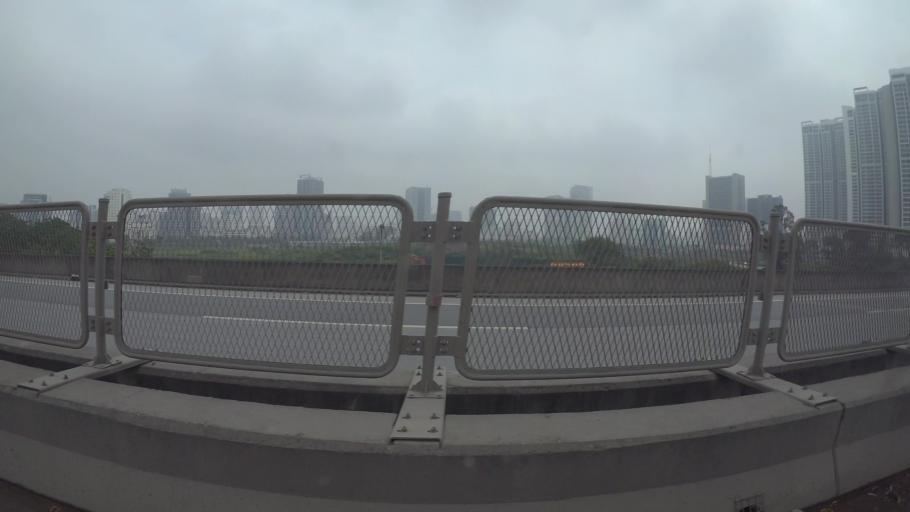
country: VN
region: Ha Noi
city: Cau Dien
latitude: 21.0230
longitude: 105.7788
